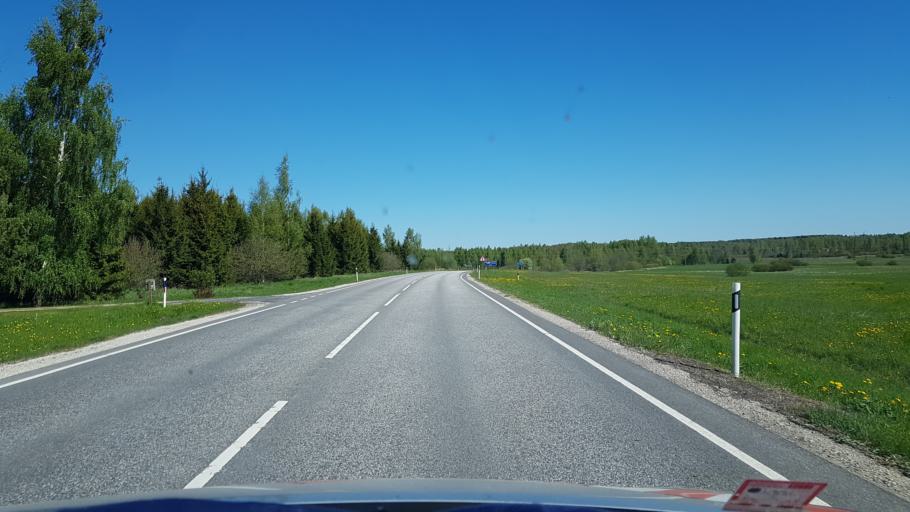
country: EE
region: Jogevamaa
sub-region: Tabivere vald
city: Tabivere
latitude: 58.6692
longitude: 26.7927
